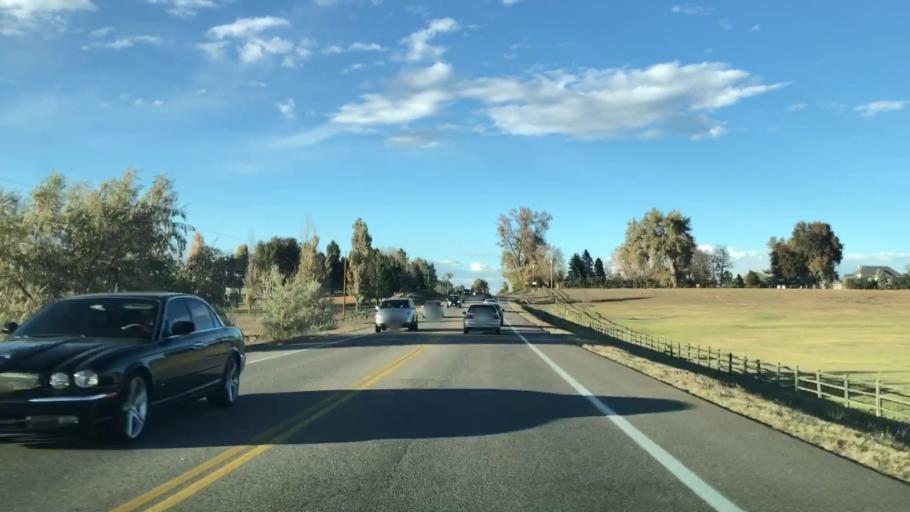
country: US
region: Colorado
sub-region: Larimer County
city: Loveland
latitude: 40.4892
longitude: -105.0393
